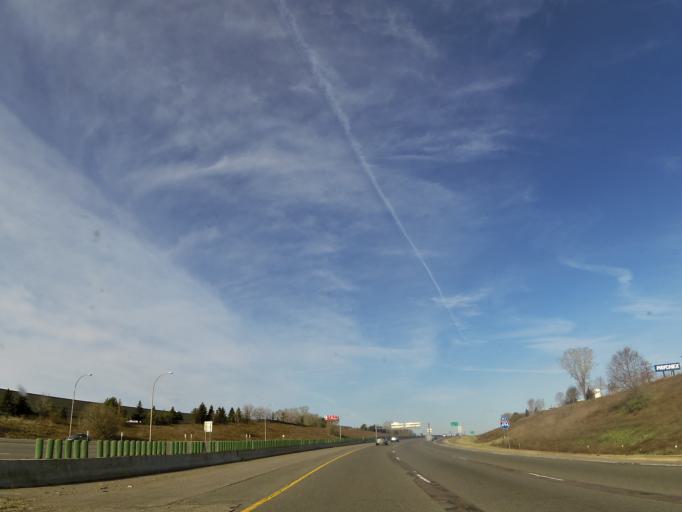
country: US
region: Minnesota
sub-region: Dakota County
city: Mendota Heights
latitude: 44.8616
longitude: -93.1524
